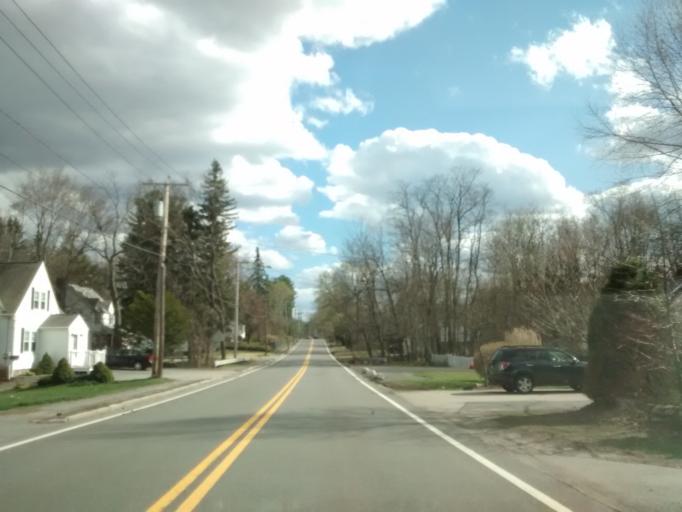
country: US
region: Massachusetts
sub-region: Worcester County
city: Worcester
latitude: 42.3025
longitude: -71.8211
